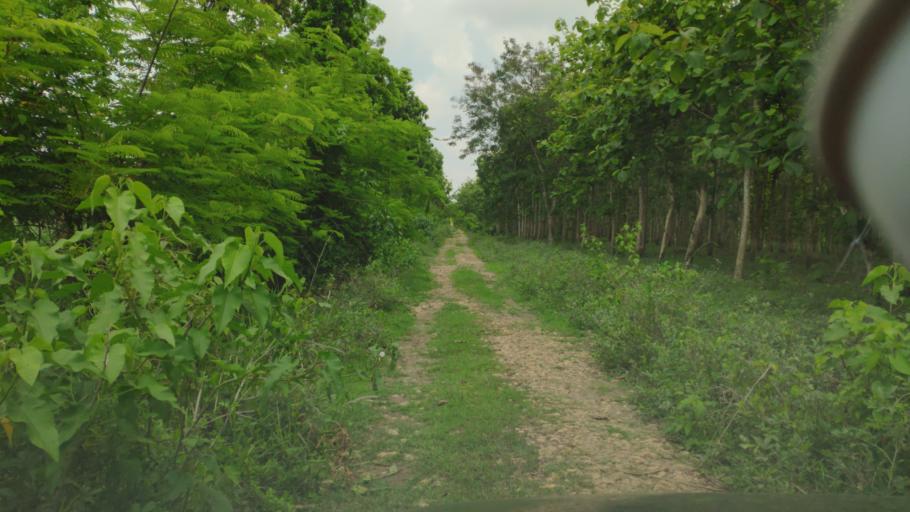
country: ID
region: Central Java
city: Padaan
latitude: -6.9359
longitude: 111.3023
